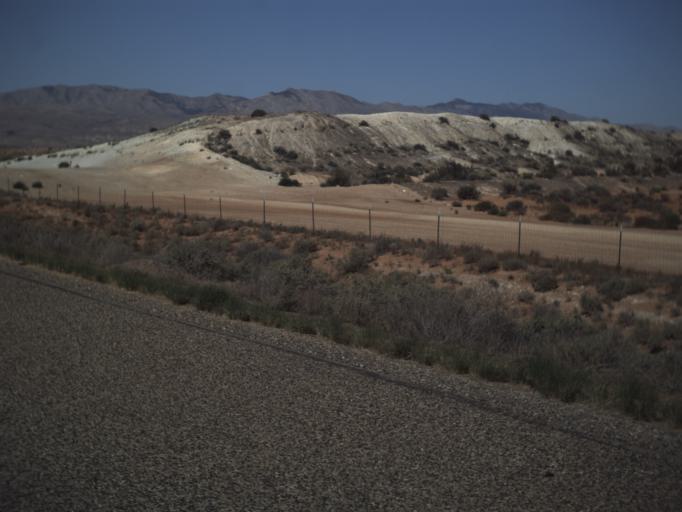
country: US
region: Utah
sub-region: Washington County
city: Saint George
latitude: 37.0008
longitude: -113.5642
